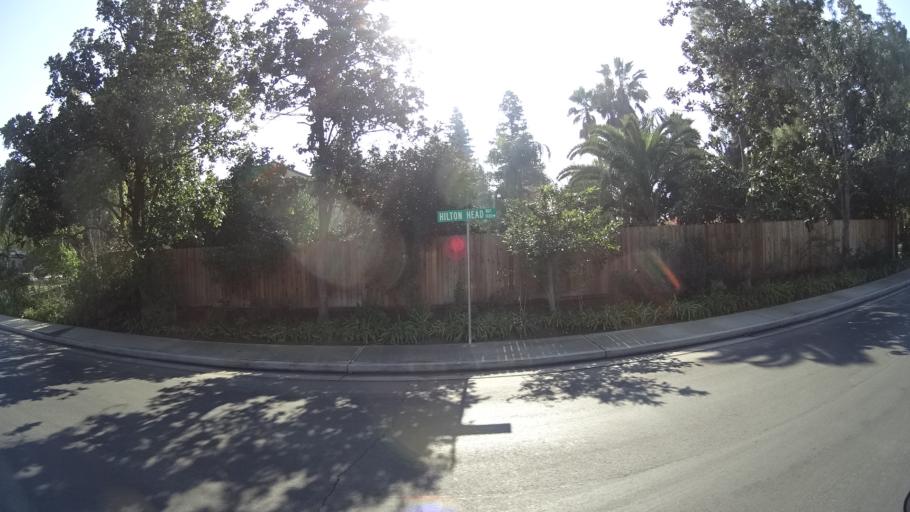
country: US
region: California
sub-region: Kern County
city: Greenacres
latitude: 35.3317
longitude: -119.0843
